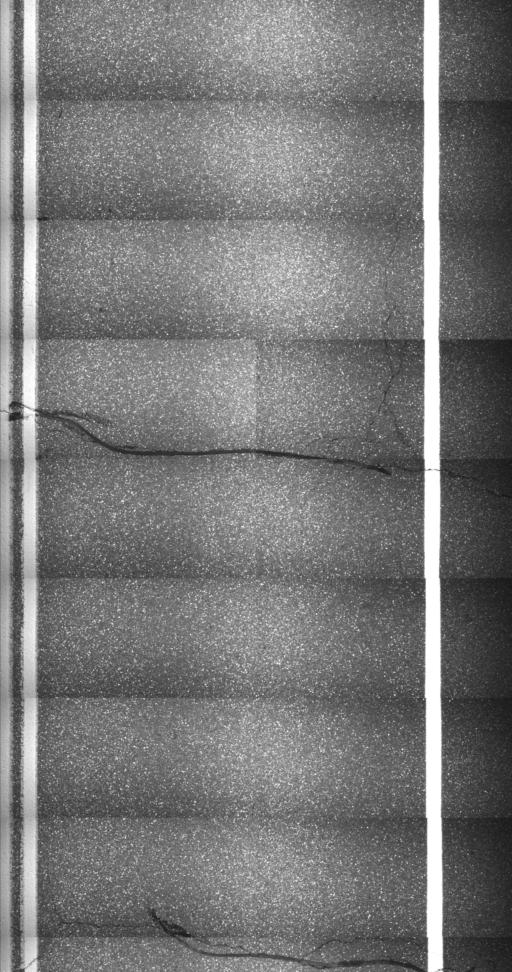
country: US
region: Vermont
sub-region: Orange County
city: Chelsea
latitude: 44.1126
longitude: -72.3157
